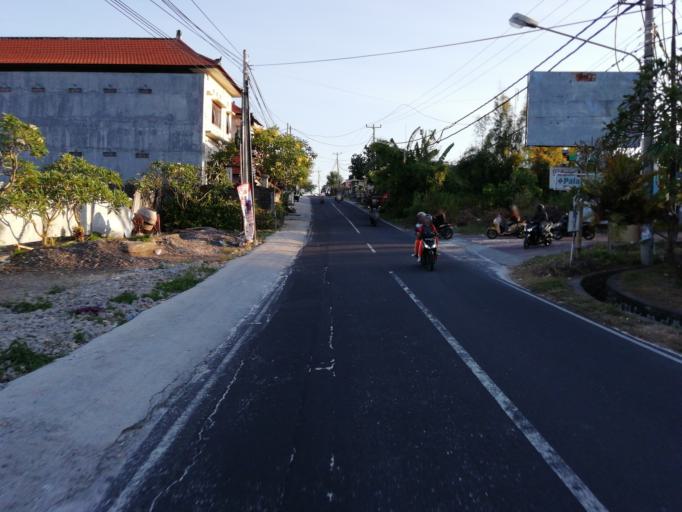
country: ID
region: Bali
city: Bualu
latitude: -8.8164
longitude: 115.1910
